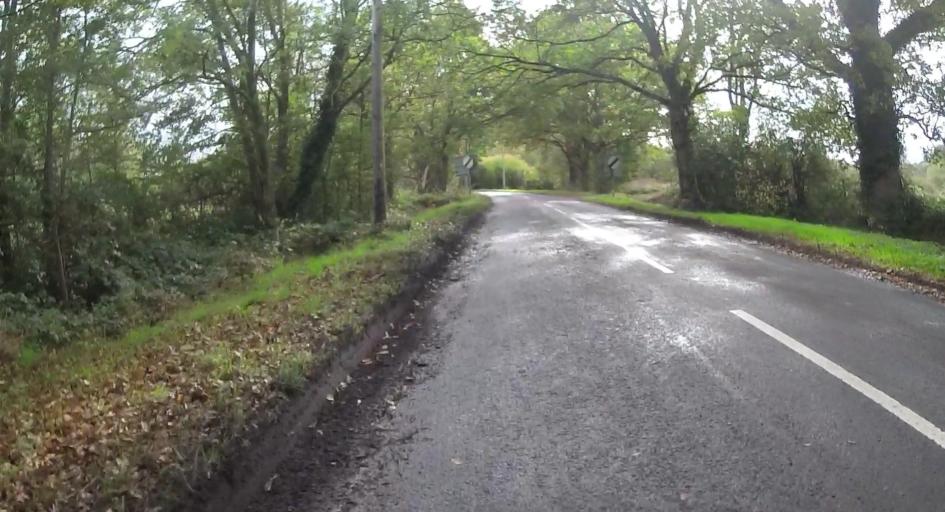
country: GB
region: England
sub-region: Hampshire
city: Odiham
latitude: 51.2831
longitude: -0.9011
